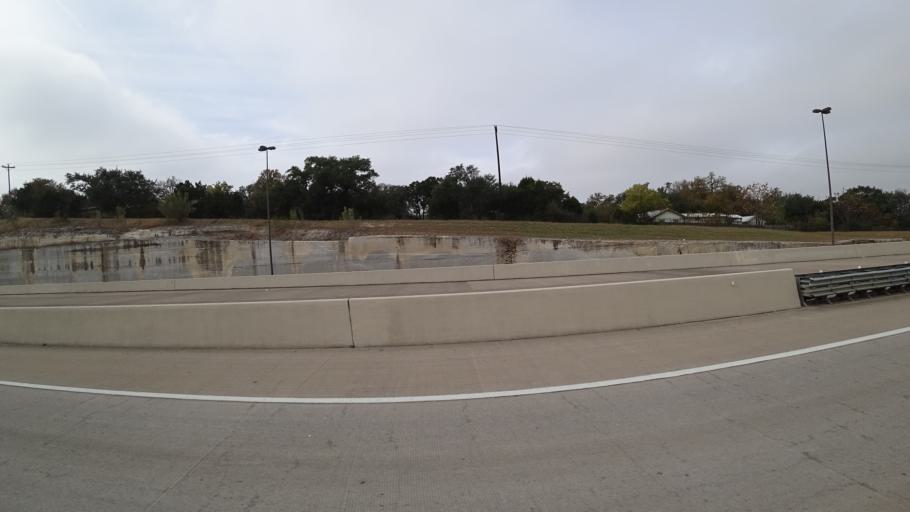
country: US
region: Texas
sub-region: Williamson County
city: Cedar Park
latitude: 30.5157
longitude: -97.8139
